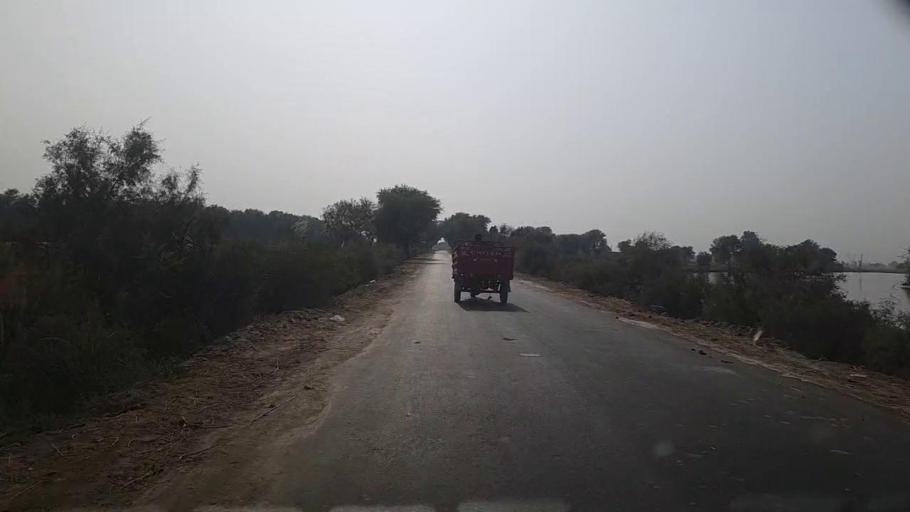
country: PK
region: Sindh
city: Kashmor
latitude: 28.4110
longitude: 69.5644
